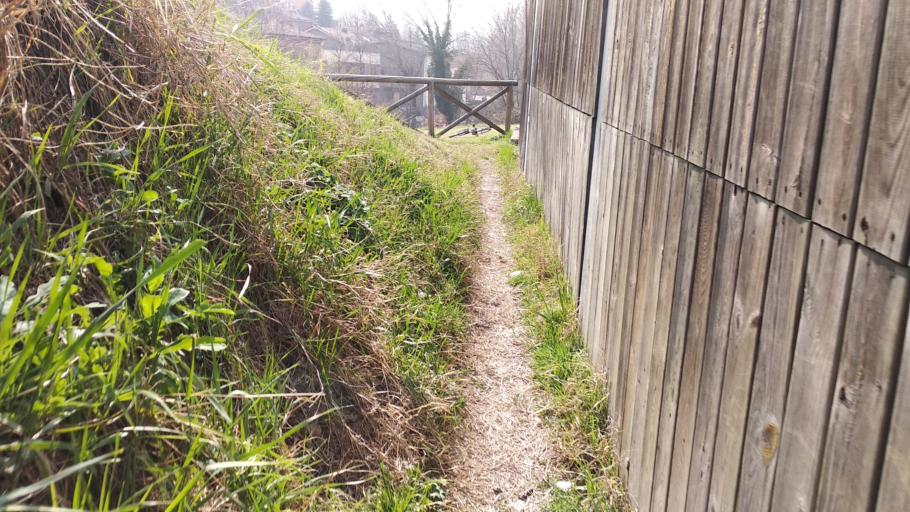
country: IT
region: Emilia-Romagna
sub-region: Provincia di Bologna
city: Ponticella
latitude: 44.4596
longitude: 11.3755
